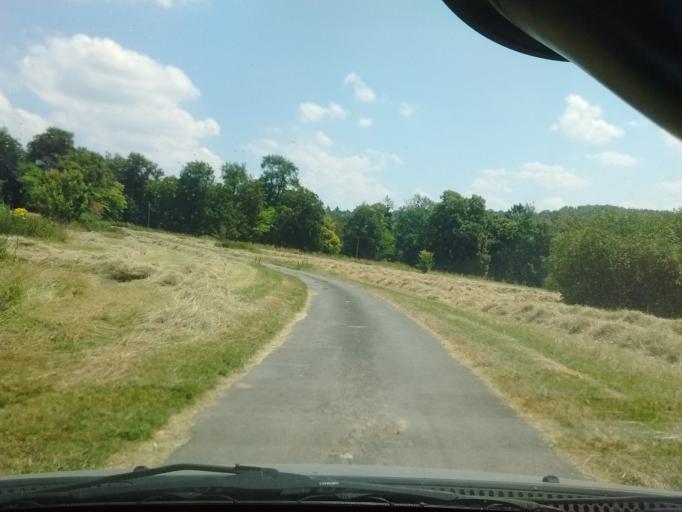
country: FR
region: Ile-de-France
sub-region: Departement de Seine-et-Marne
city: Saint-Sauveur-sur-Ecole
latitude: 48.5127
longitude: 2.5441
